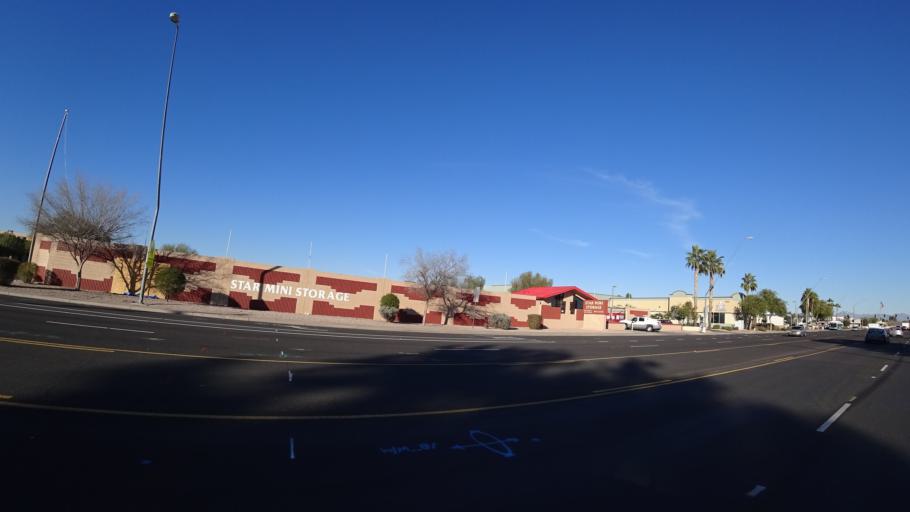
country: US
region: Arizona
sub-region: Maricopa County
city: Gilbert
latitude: 33.3935
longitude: -111.7911
